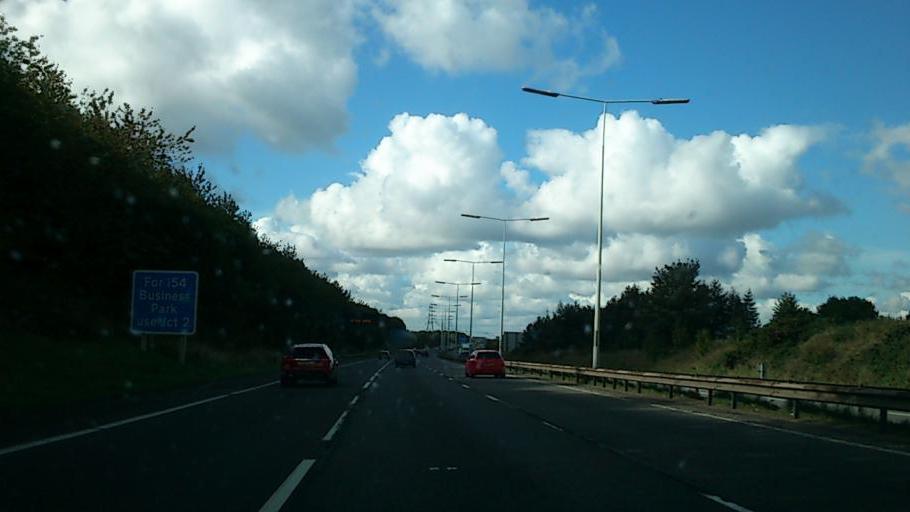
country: GB
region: England
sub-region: Staffordshire
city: Featherstone
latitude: 52.6391
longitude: -2.0961
